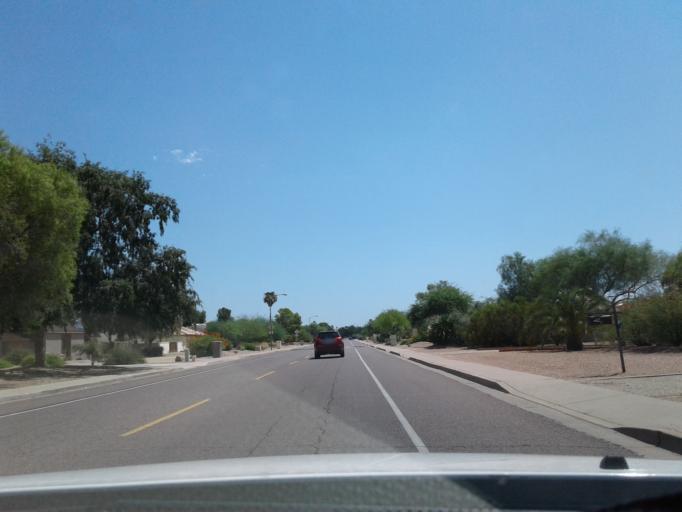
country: US
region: Arizona
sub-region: Maricopa County
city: Paradise Valley
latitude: 33.5899
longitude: -111.9821
